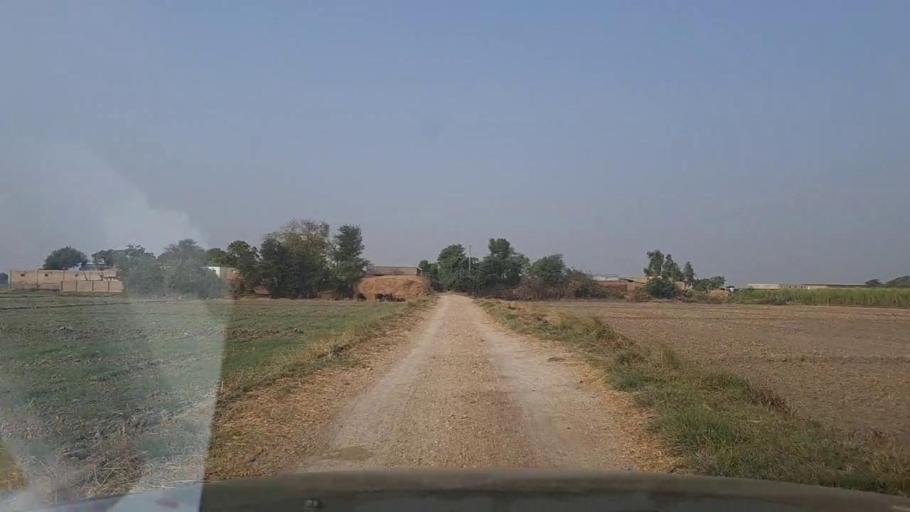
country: PK
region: Sindh
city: Bulri
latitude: 24.9405
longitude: 68.2800
